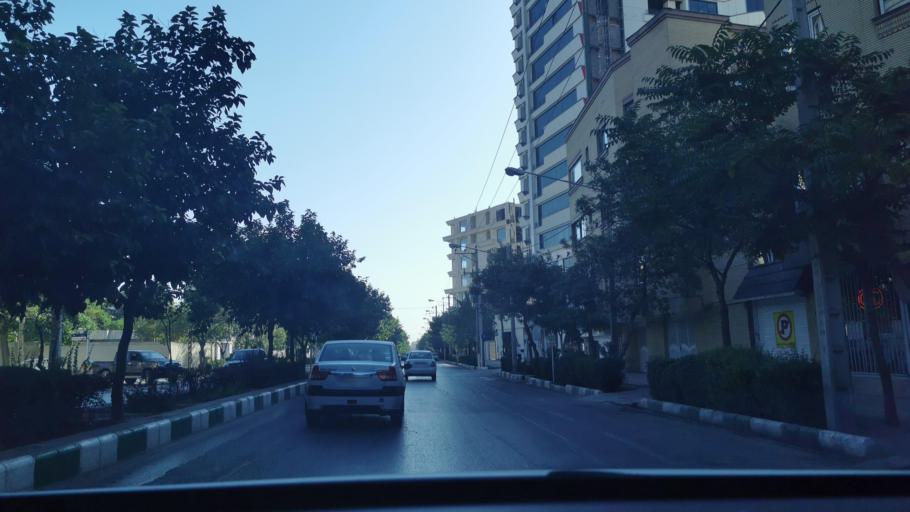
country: IR
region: Razavi Khorasan
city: Mashhad
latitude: 36.3142
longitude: 59.5171
